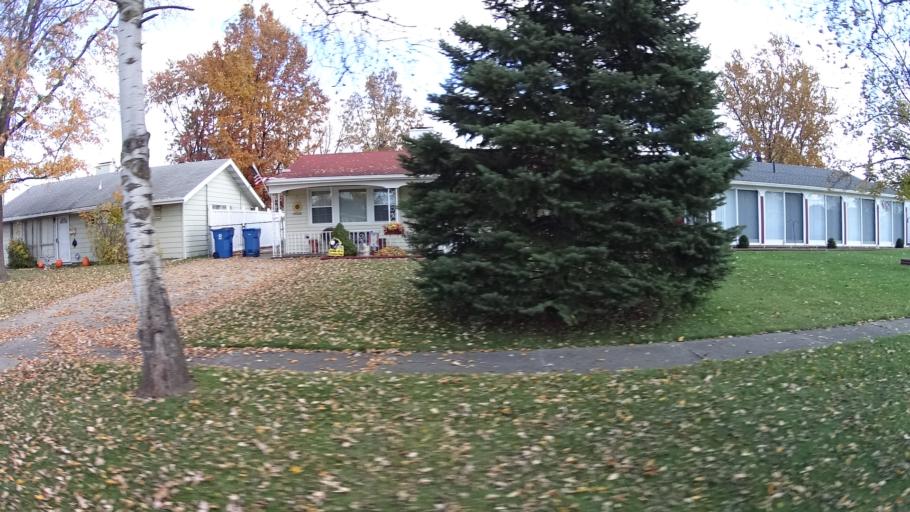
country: US
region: Ohio
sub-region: Lorain County
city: Sheffield
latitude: 41.4310
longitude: -82.1130
